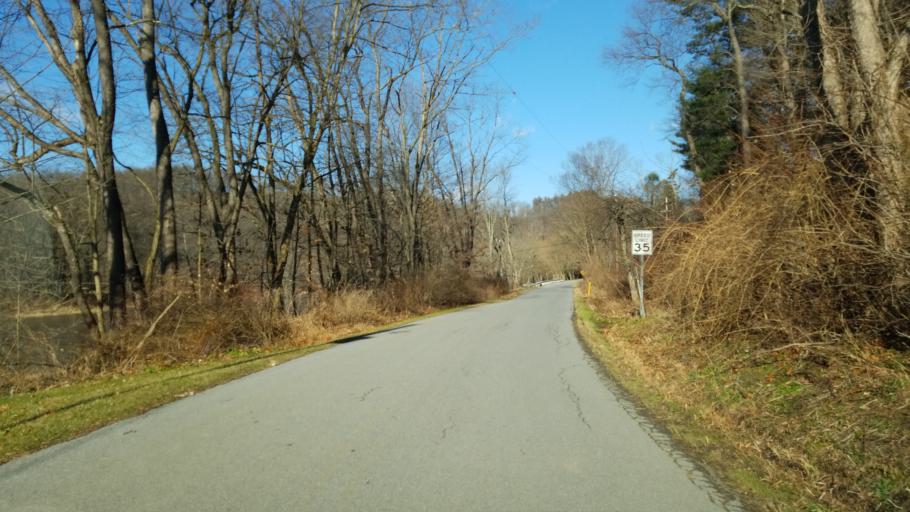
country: US
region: Pennsylvania
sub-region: Clearfield County
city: Curwensville
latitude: 40.9783
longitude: -78.4932
